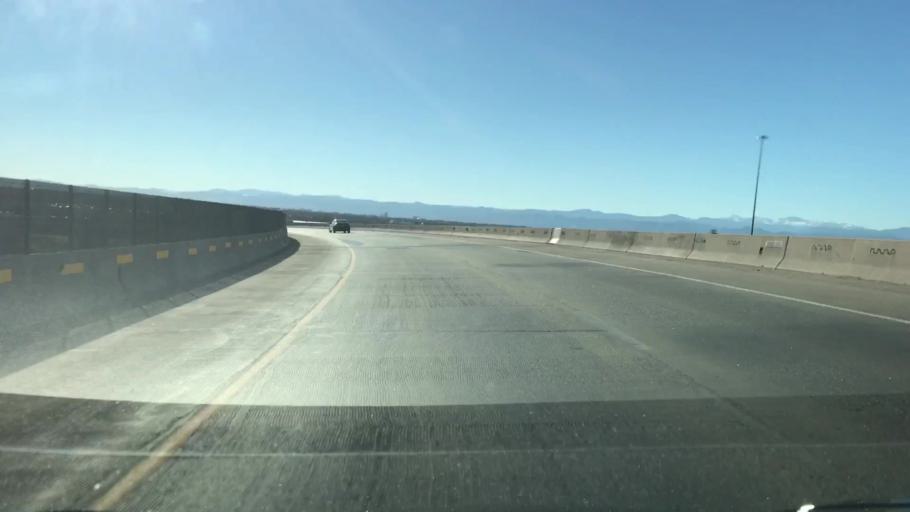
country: US
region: Colorado
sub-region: Adams County
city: Aurora
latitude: 39.7714
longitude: -104.8272
